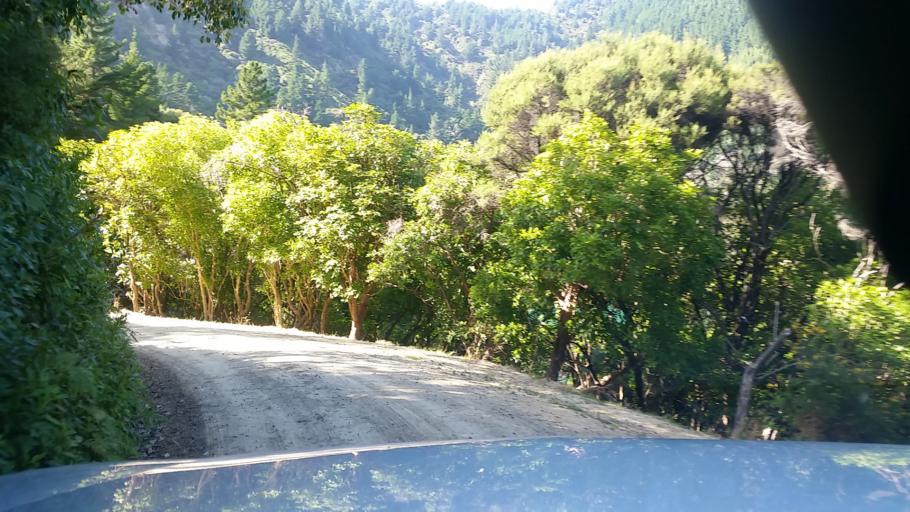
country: NZ
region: Marlborough
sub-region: Marlborough District
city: Picton
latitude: -41.3123
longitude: 174.1720
